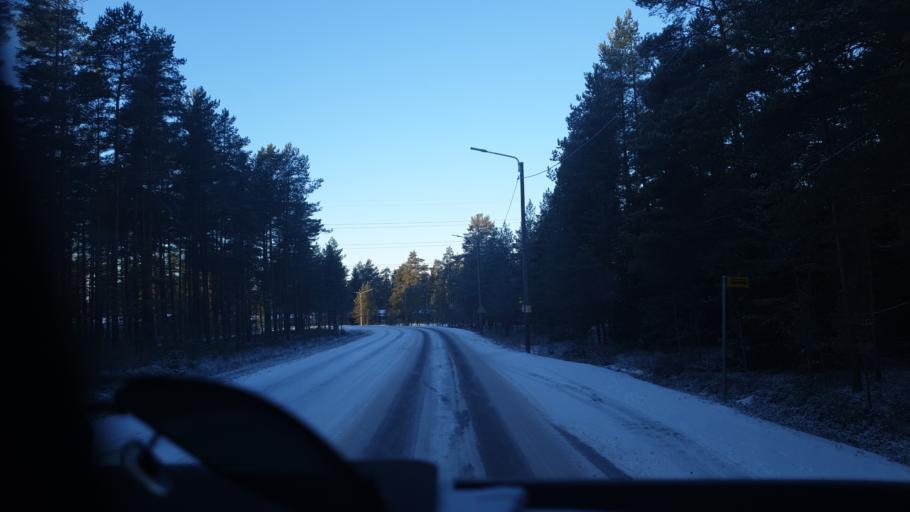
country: FI
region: Central Ostrobothnia
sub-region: Kokkola
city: Kokkola
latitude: 63.8253
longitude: 23.0917
